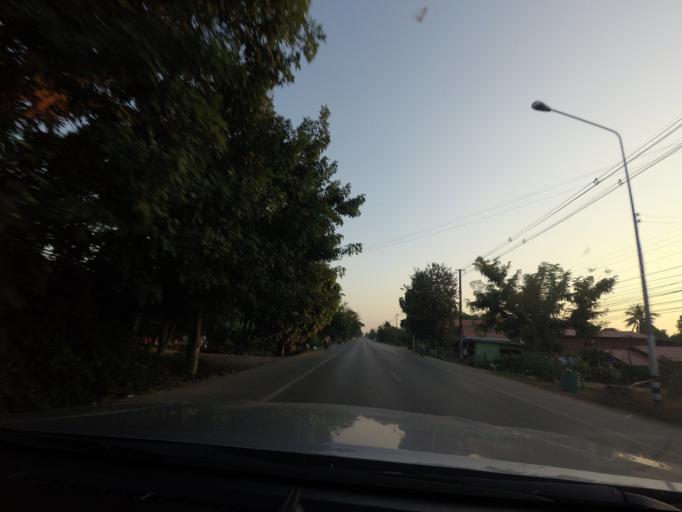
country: TH
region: Sukhothai
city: Si Samrong
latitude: 17.1276
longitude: 99.8505
